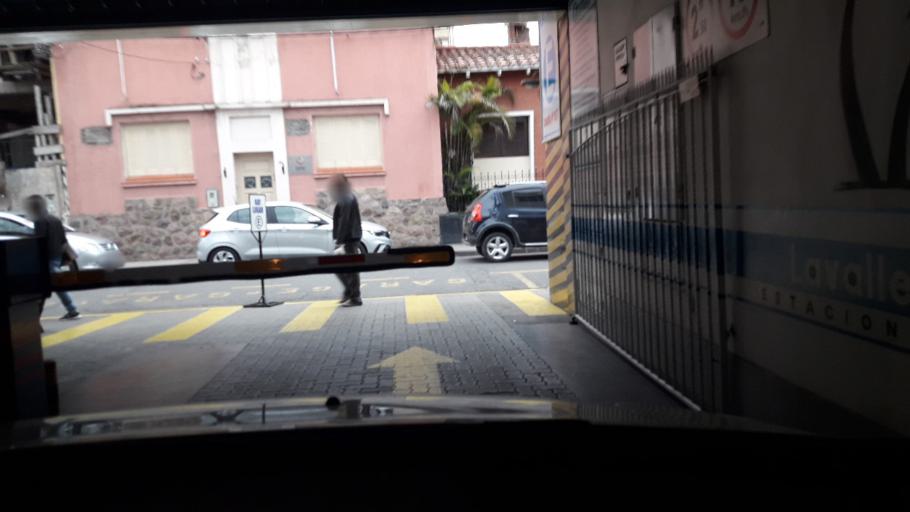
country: AR
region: Jujuy
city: San Salvador de Jujuy
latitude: -24.1833
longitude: -65.3028
